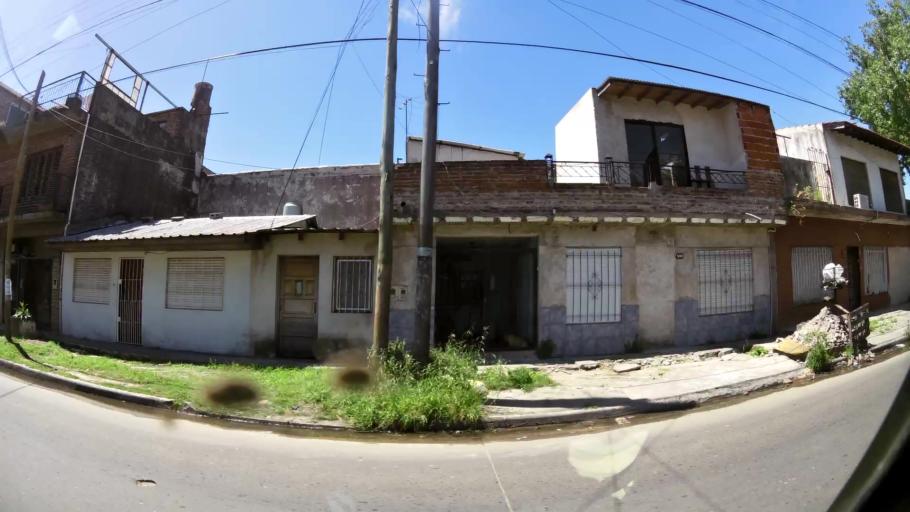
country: AR
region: Buenos Aires
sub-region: Partido de Quilmes
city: Quilmes
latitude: -34.7275
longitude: -58.3091
